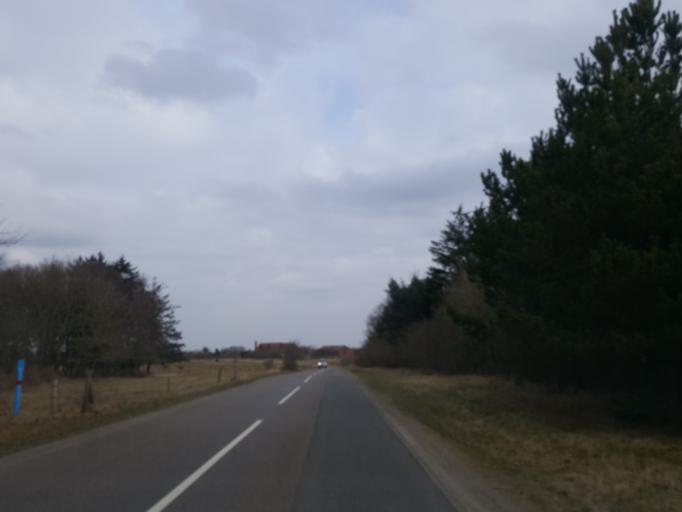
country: DK
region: Central Jutland
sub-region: Holstebro Kommune
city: Ulfborg
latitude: 56.3964
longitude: 8.2289
